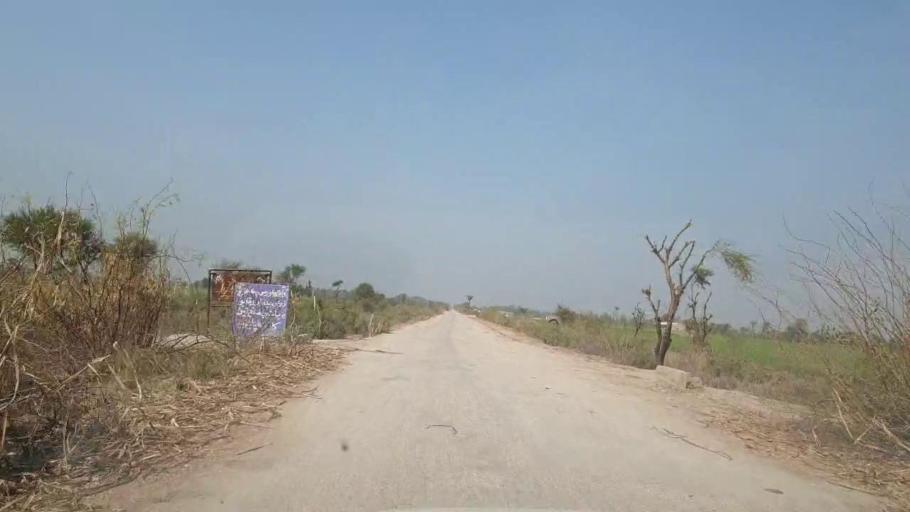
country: PK
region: Sindh
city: Mirpur Khas
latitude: 25.6762
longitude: 69.1551
